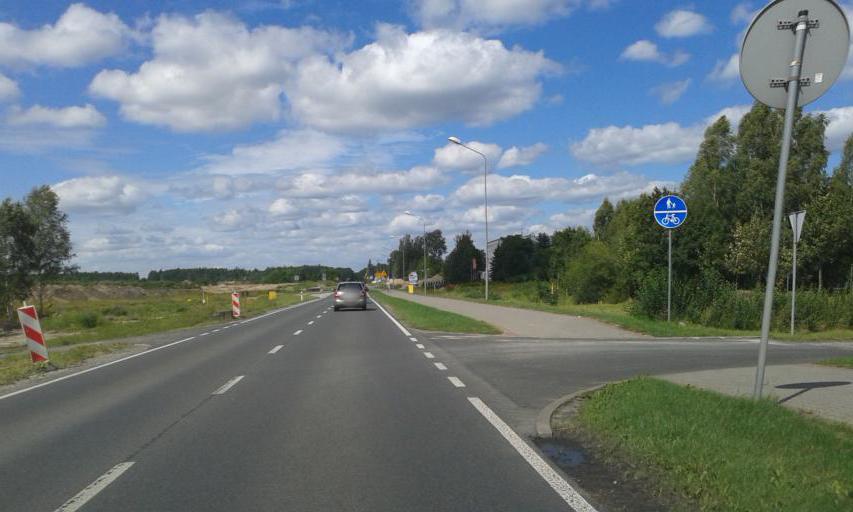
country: PL
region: West Pomeranian Voivodeship
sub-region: Powiat walecki
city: Walcz
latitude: 53.2917
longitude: 16.4583
